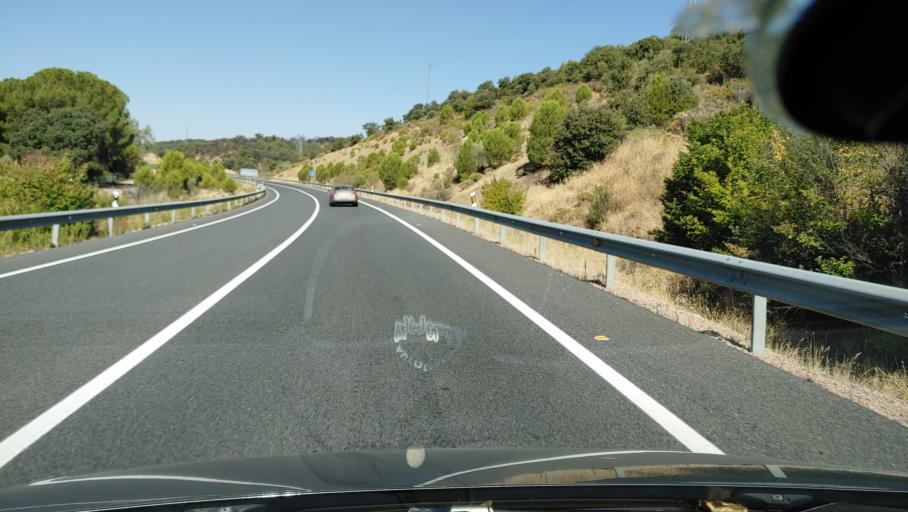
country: ES
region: Andalusia
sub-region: Province of Cordoba
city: Villaharta
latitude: 38.1299
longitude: -4.9095
